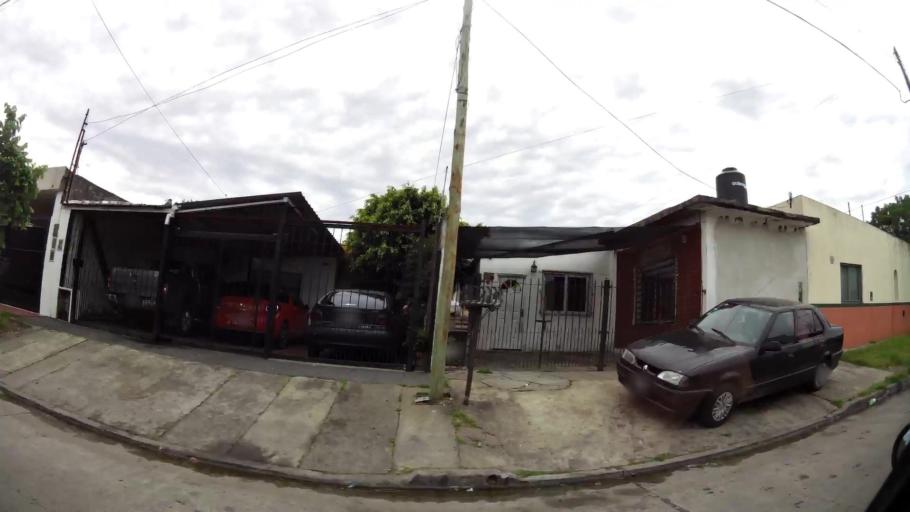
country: AR
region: Buenos Aires
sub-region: Partido de Quilmes
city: Quilmes
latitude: -34.7551
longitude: -58.2230
